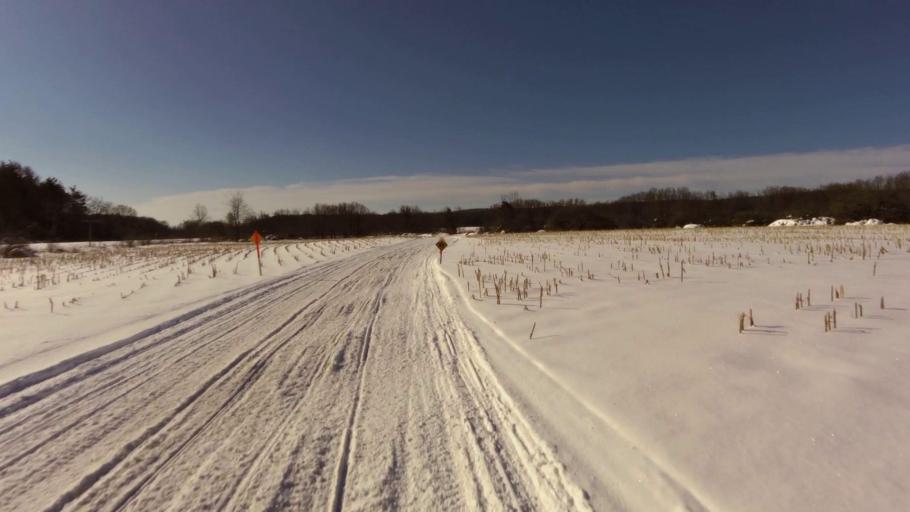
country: US
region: New York
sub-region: Cattaraugus County
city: Franklinville
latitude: 42.3981
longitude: -78.4731
